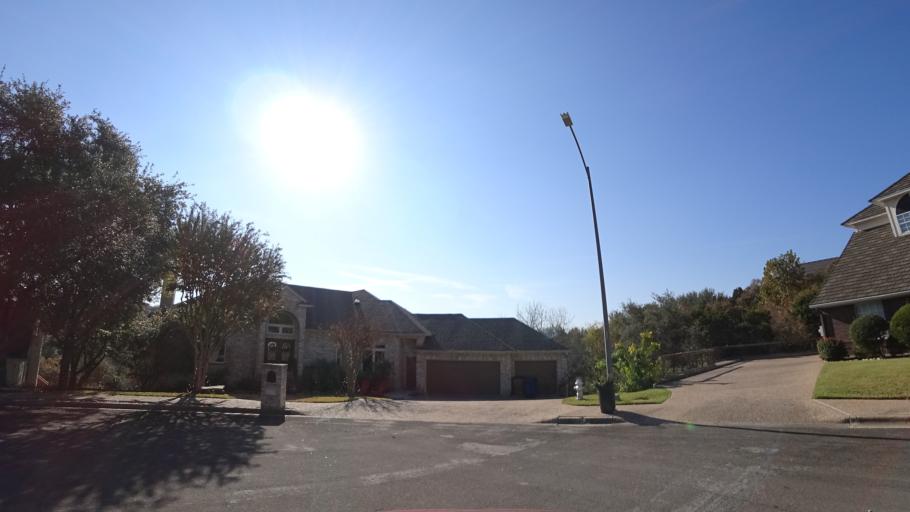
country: US
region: Texas
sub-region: Williamson County
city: Jollyville
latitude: 30.3965
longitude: -97.7648
